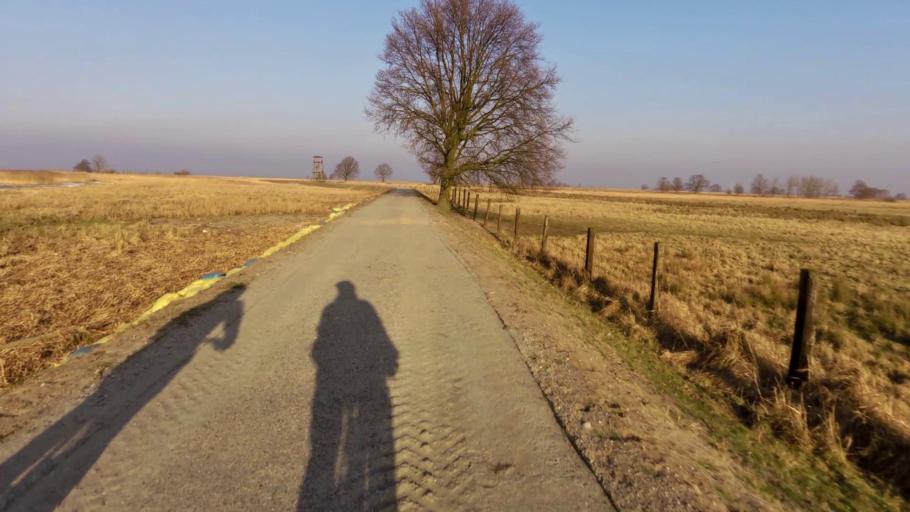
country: PL
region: West Pomeranian Voivodeship
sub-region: Powiat kamienski
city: Wolin
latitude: 53.7521
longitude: 14.5596
